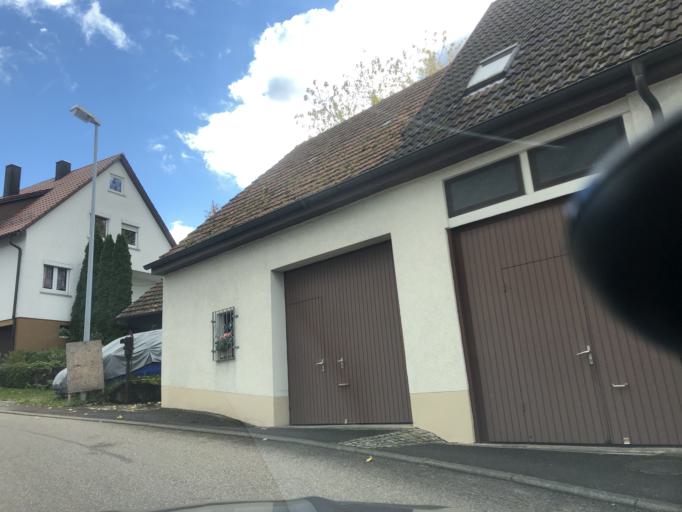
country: DE
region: Baden-Wuerttemberg
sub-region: Regierungsbezirk Stuttgart
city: Weinstadt-Endersbach
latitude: 48.7908
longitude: 9.4093
